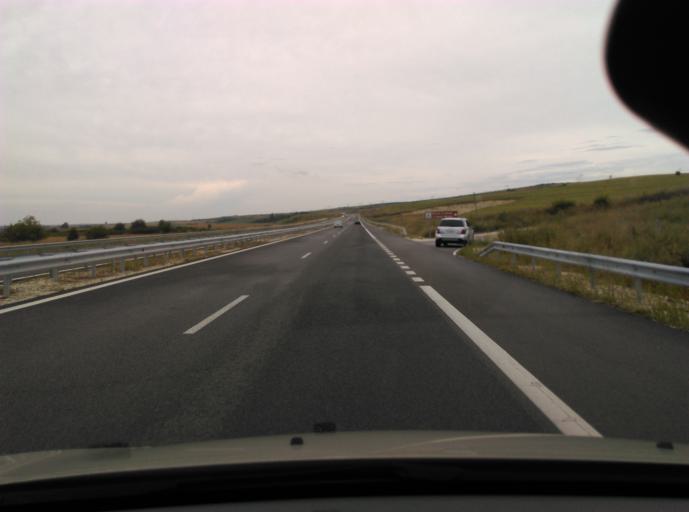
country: BG
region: Stara Zagora
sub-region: Obshtina Chirpan
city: Chirpan
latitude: 42.1058
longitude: 25.4186
